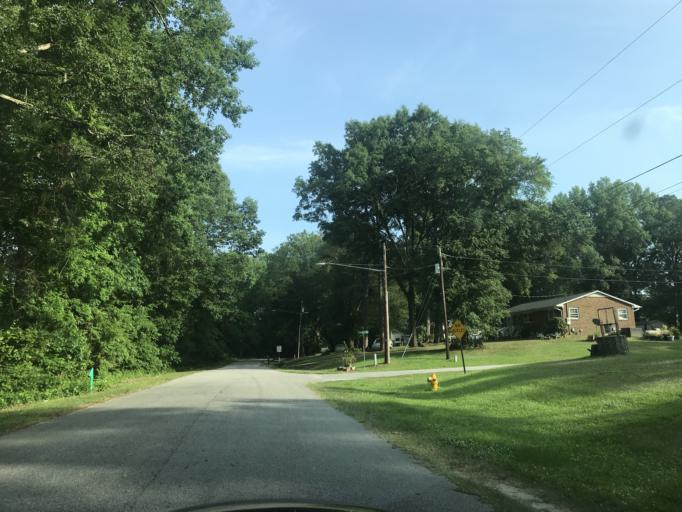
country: US
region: North Carolina
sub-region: Wake County
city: Garner
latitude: 35.7442
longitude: -78.5714
